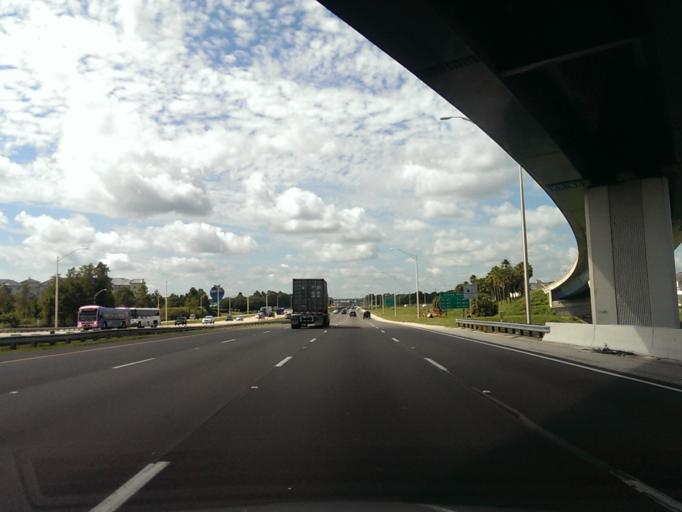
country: US
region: Florida
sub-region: Orange County
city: Williamsburg
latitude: 28.4097
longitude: -81.4760
